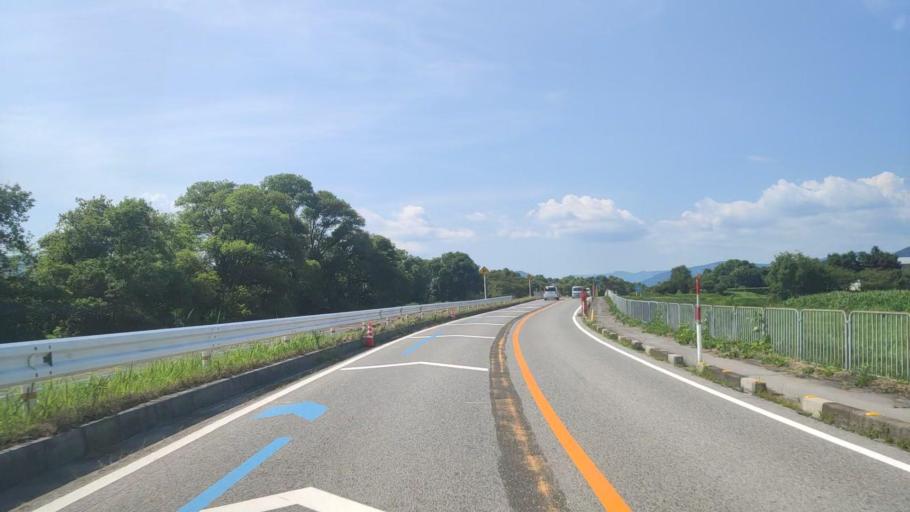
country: JP
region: Shiga Prefecture
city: Nagahama
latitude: 35.4406
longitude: 136.1904
